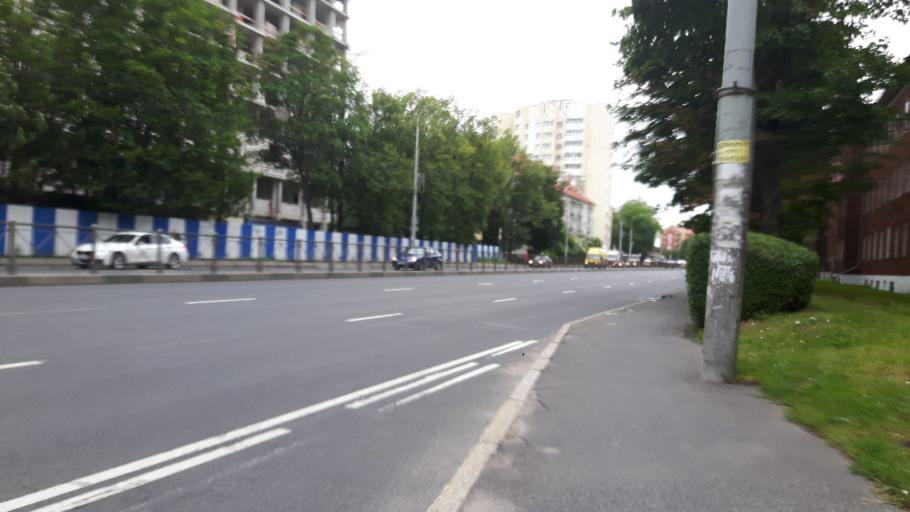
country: RU
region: Kaliningrad
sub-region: Gorod Kaliningrad
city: Kaliningrad
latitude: 54.7341
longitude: 20.4844
